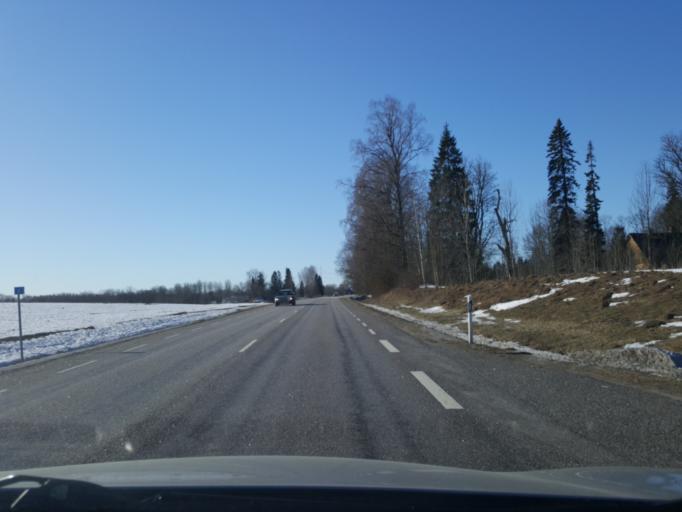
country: EE
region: Viljandimaa
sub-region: Viiratsi vald
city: Viiratsi
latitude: 58.3984
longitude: 25.6461
